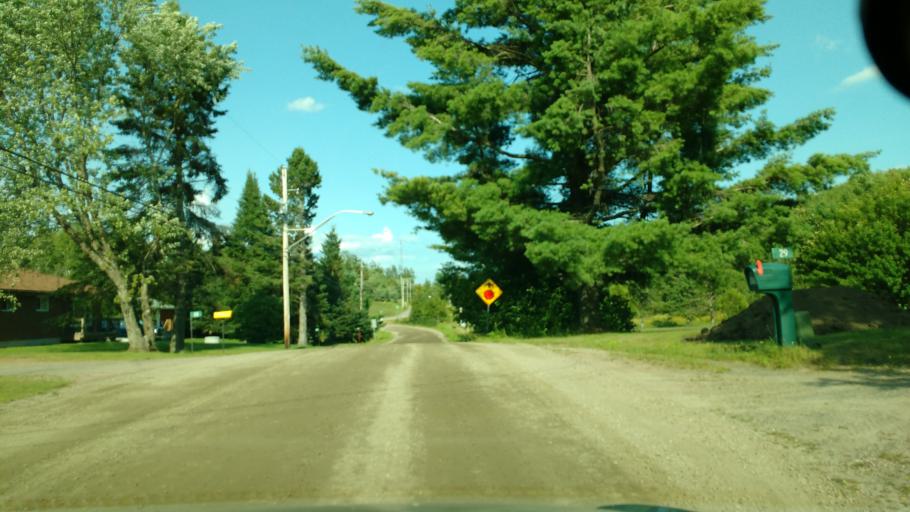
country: CA
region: Ontario
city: Powassan
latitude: 46.1844
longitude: -79.2882
